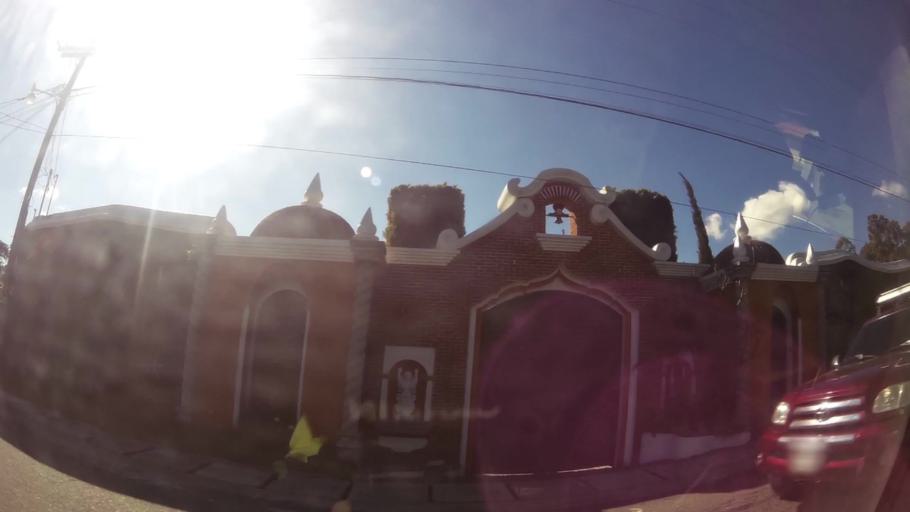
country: GT
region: Sacatepequez
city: Santa Lucia Milpas Altas
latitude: 14.5685
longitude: -90.6393
